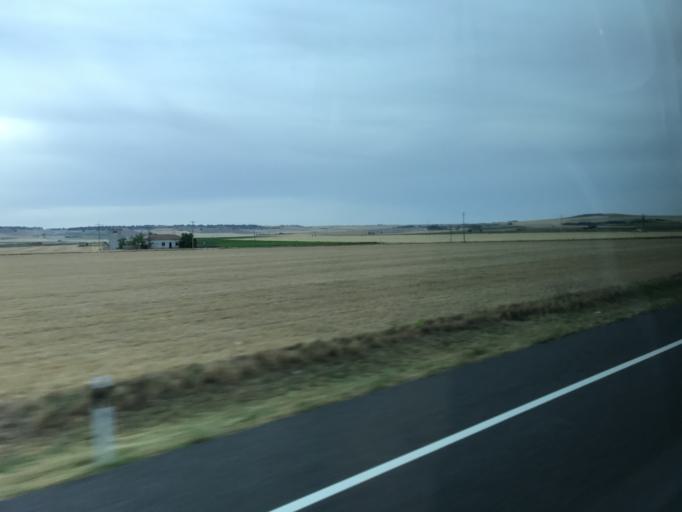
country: ES
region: Castille and Leon
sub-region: Provincia de Segovia
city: Tolocirio
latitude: 41.1386
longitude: -4.6486
